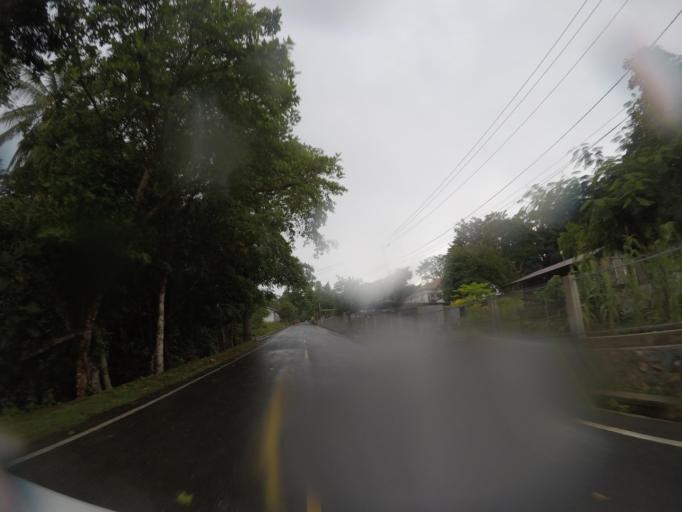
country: TL
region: Bobonaro
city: Maliana
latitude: -8.9686
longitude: 125.0404
